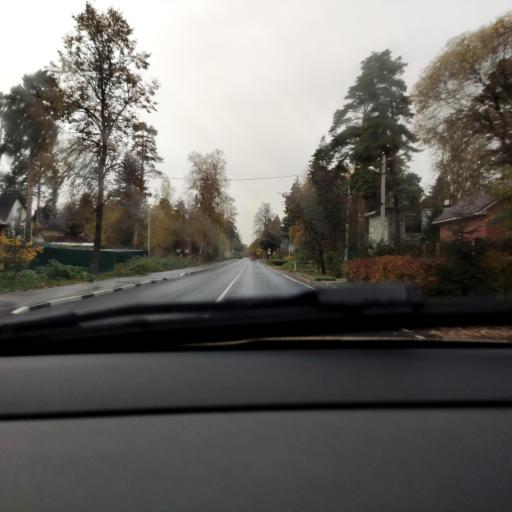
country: RU
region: Moskovskaya
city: Mamontovka
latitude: 55.9739
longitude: 37.8431
